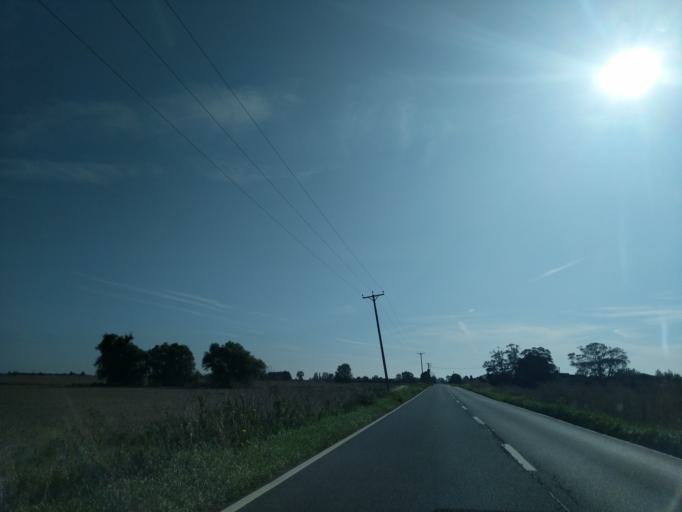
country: GB
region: England
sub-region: Lincolnshire
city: Bourne
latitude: 52.7720
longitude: -0.3130
